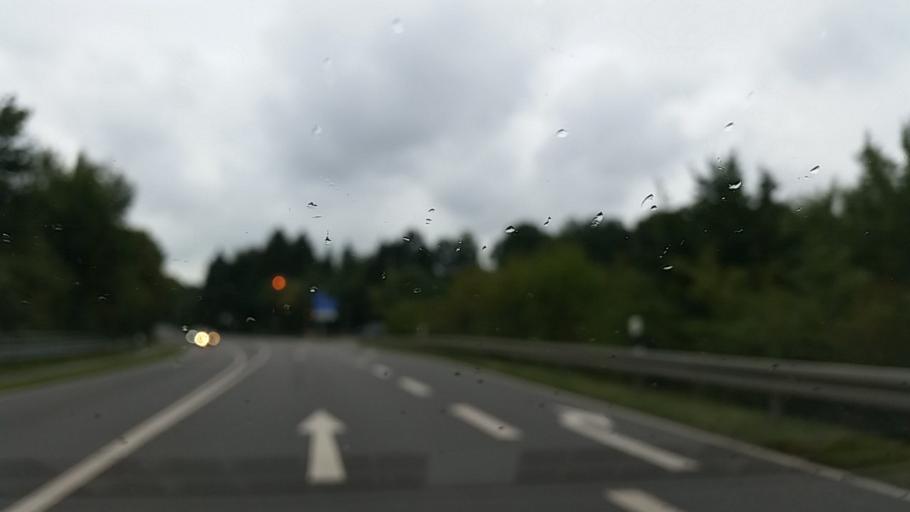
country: DE
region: Lower Saxony
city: Hasbergen
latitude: 52.2689
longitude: 7.9618
